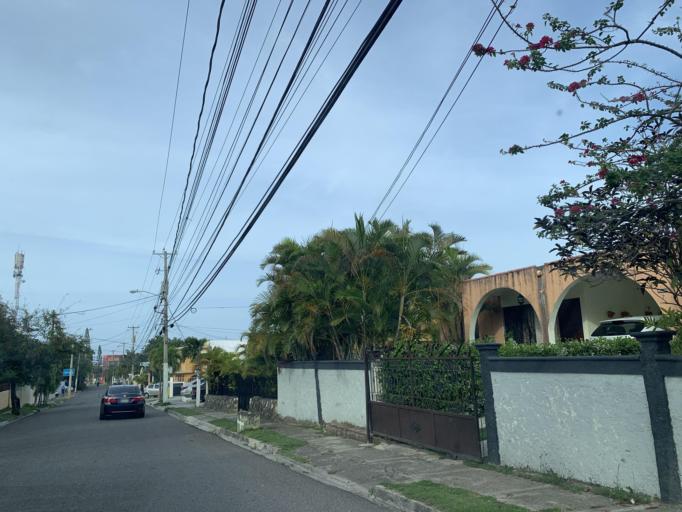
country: DO
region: Puerto Plata
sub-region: Puerto Plata
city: Puerto Plata
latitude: 19.7809
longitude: -70.6802
